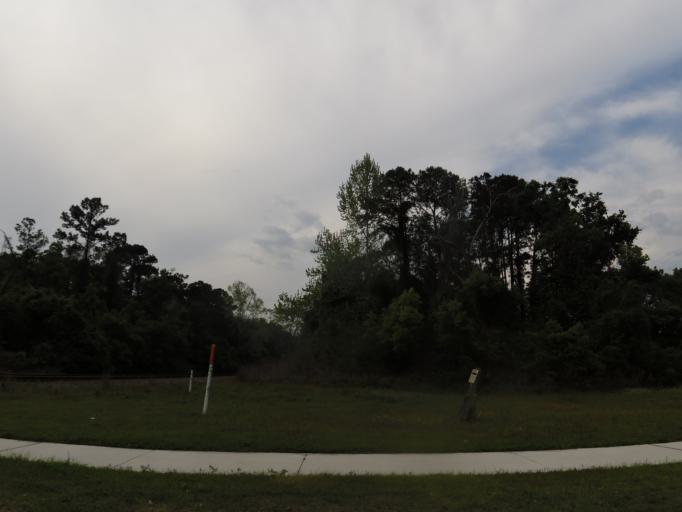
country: US
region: Florida
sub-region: Nassau County
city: Hilliard
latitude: 30.6900
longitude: -81.9196
